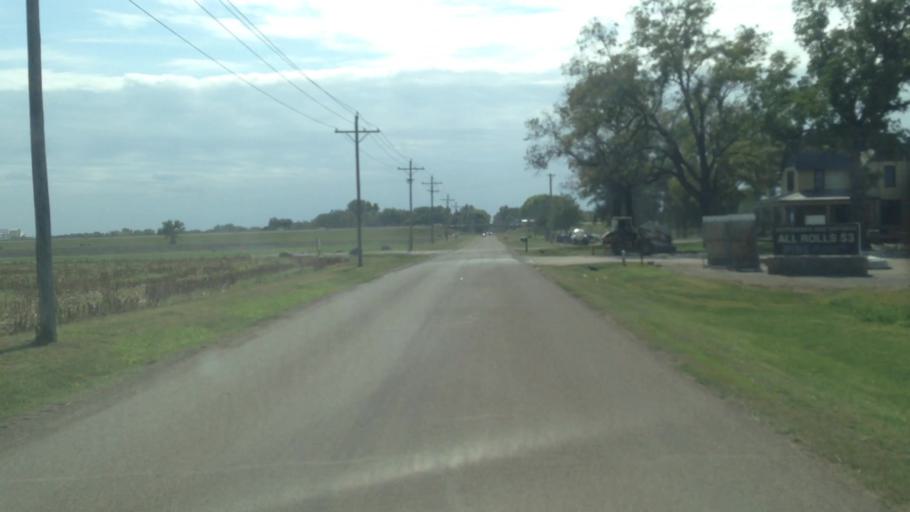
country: US
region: Kansas
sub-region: Douglas County
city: Lawrence
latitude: 38.9990
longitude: -95.2241
